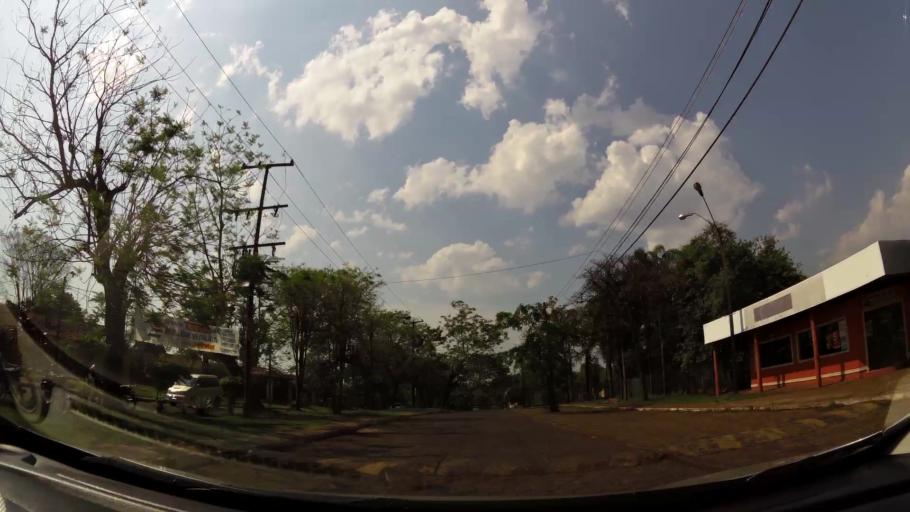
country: PY
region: Alto Parana
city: Presidente Franco
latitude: -25.5172
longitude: -54.6363
